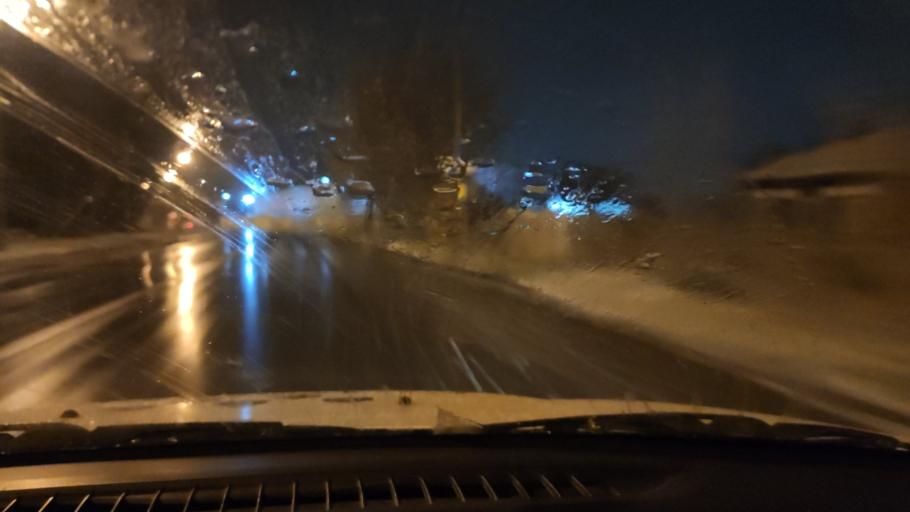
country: RU
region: Perm
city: Kondratovo
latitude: 57.9505
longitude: 56.1385
